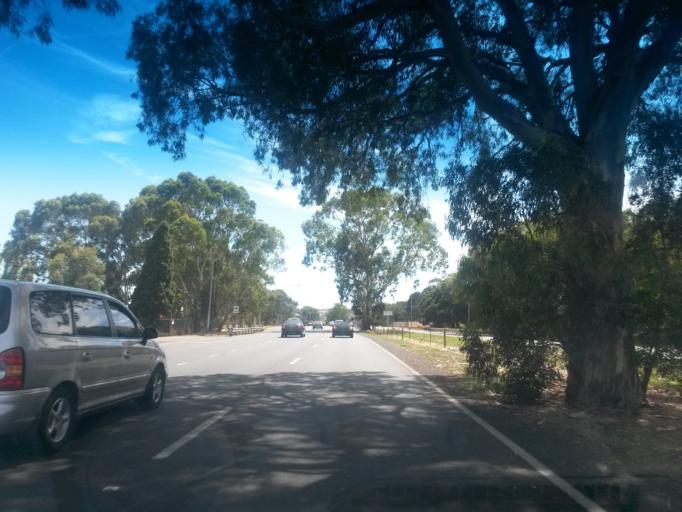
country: AU
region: South Australia
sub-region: Salisbury
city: Salisbury
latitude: -34.7682
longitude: 138.6677
